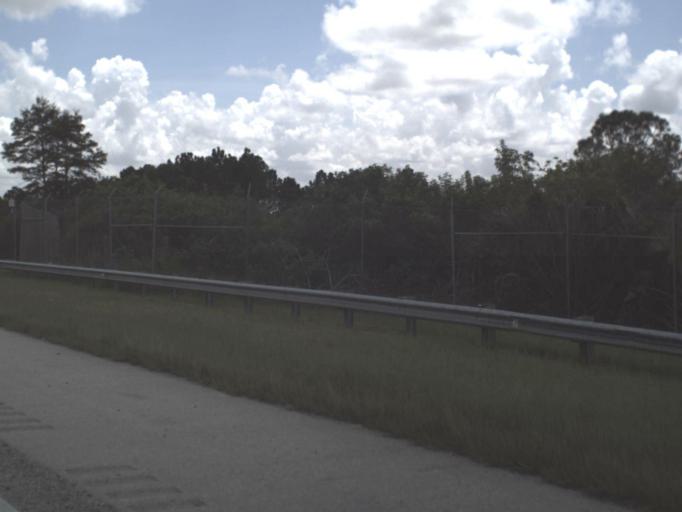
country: US
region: Florida
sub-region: Collier County
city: Immokalee
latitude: 26.1707
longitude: -80.9641
